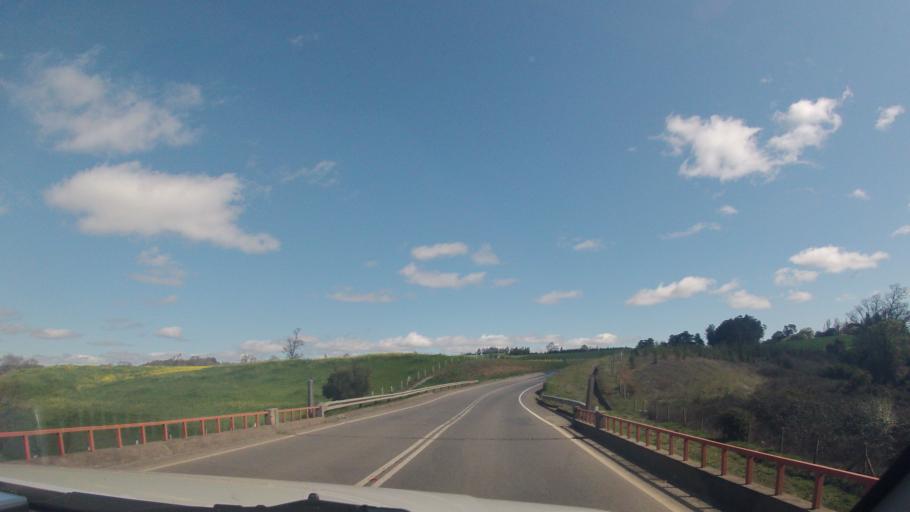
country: CL
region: Araucania
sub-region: Provincia de Malleco
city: Traiguen
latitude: -38.2194
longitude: -72.7117
